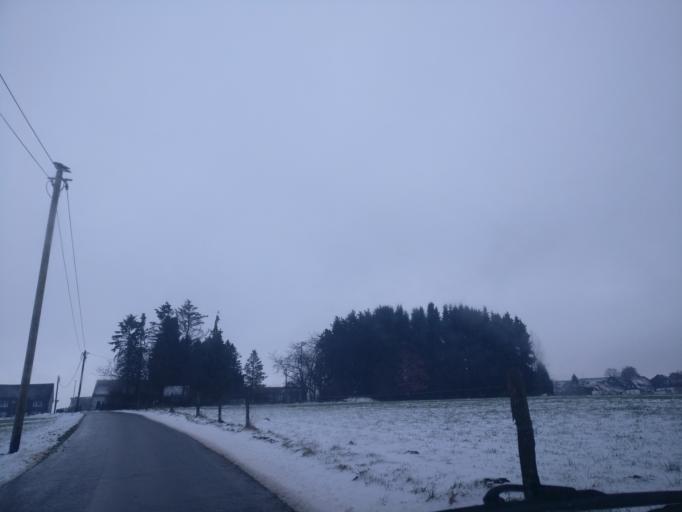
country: DE
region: North Rhine-Westphalia
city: Radevormwald
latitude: 51.1945
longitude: 7.3341
